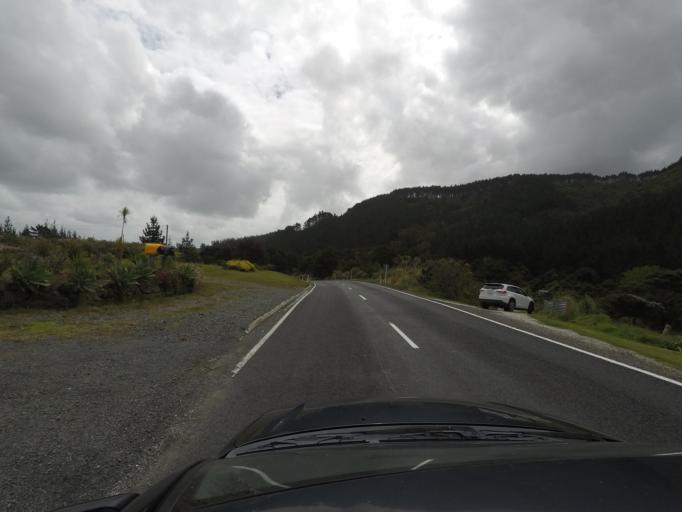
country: NZ
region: Auckland
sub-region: Auckland
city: Parakai
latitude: -36.5012
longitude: 174.4805
